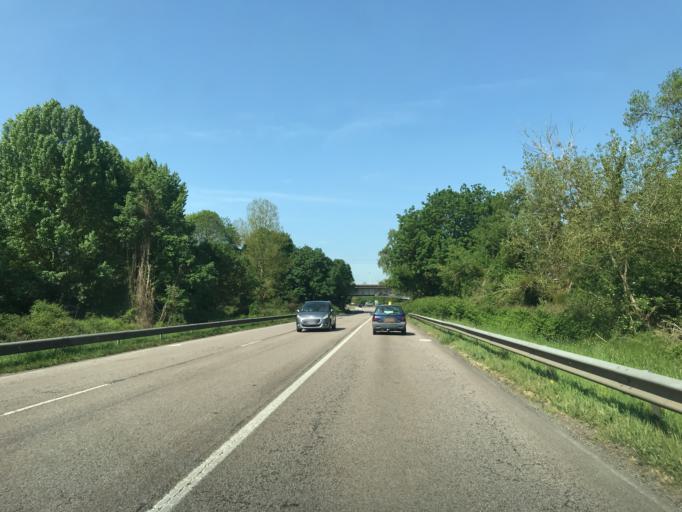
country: FR
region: Haute-Normandie
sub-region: Departement de la Seine-Maritime
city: Tourville-la-Riviere
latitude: 49.3342
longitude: 1.1052
